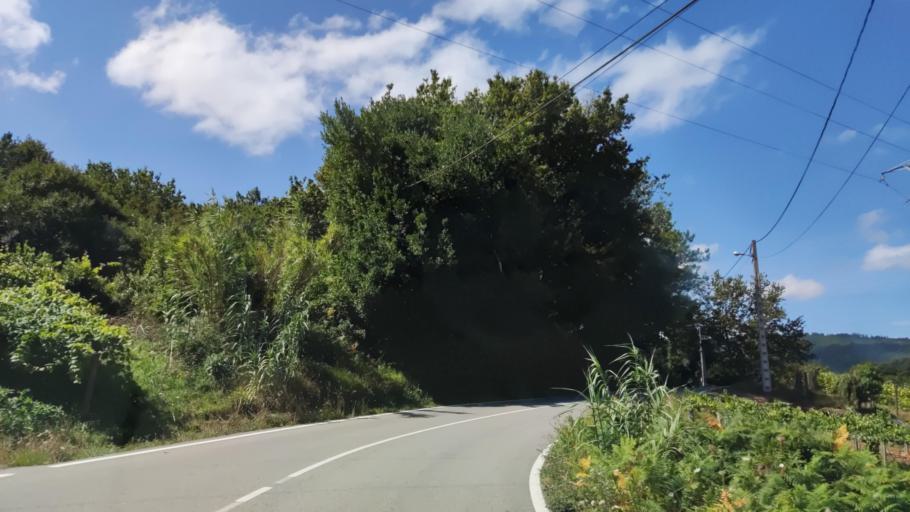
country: ES
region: Galicia
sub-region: Provincia da Coruna
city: Rianxo
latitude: 42.6949
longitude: -8.8412
